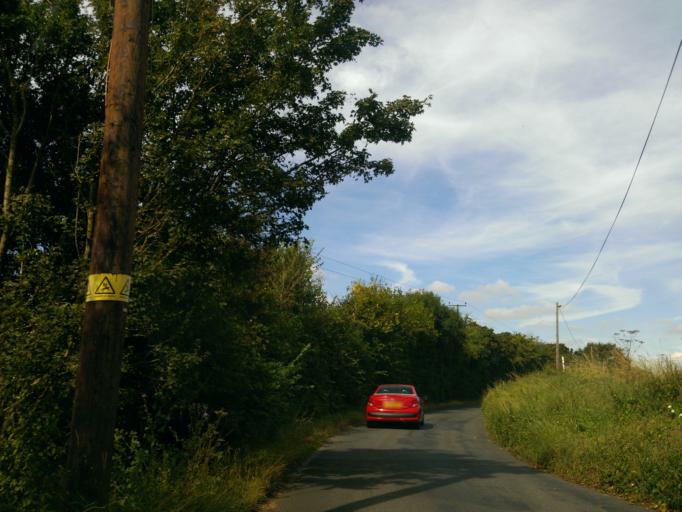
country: GB
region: England
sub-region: Essex
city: Sible Hedingham
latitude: 51.9740
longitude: 0.6193
